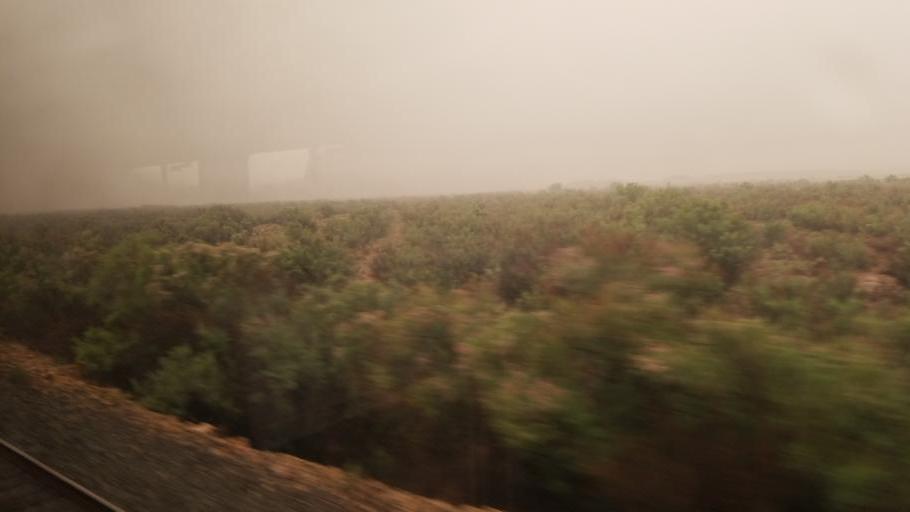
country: US
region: Arizona
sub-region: Navajo County
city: Joseph City
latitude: 34.9516
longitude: -110.3444
